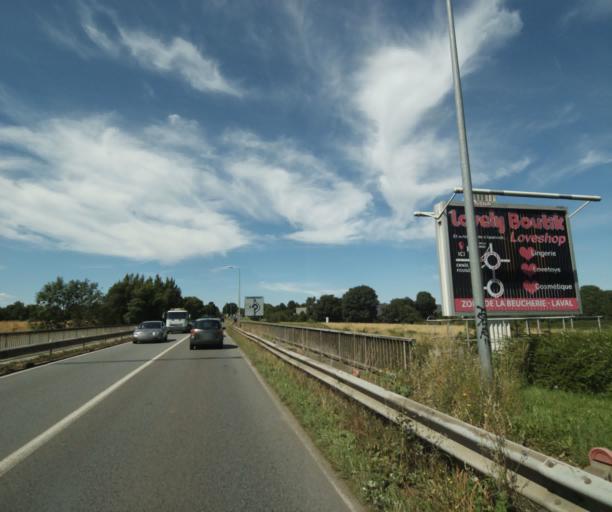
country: FR
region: Pays de la Loire
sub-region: Departement de la Mayenne
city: Change
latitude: 48.0749
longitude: -0.7956
